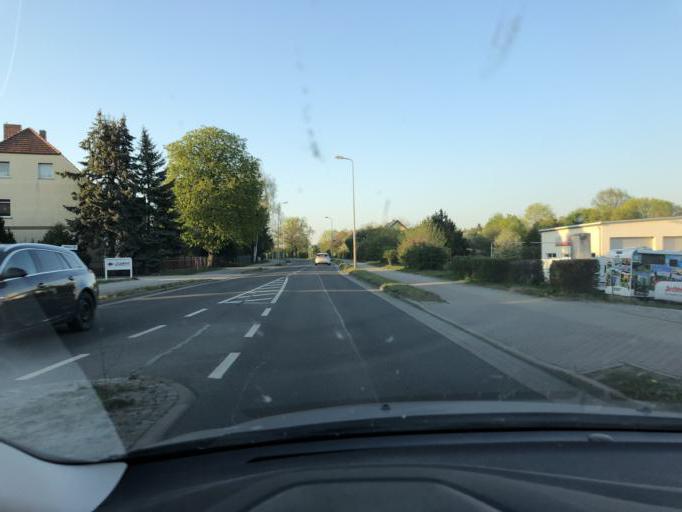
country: DE
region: Brandenburg
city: Spremberg
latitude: 51.5334
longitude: 14.3403
